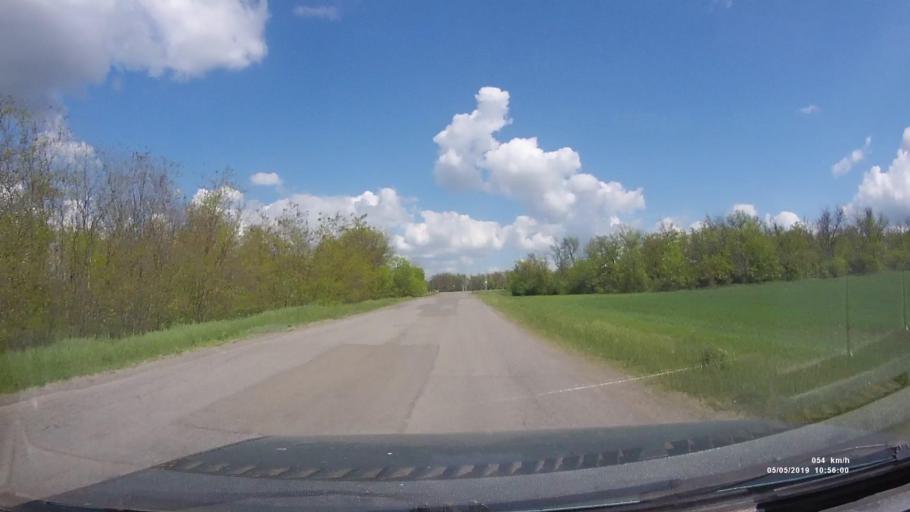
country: RU
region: Rostov
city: Ust'-Donetskiy
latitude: 47.6705
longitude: 40.8198
